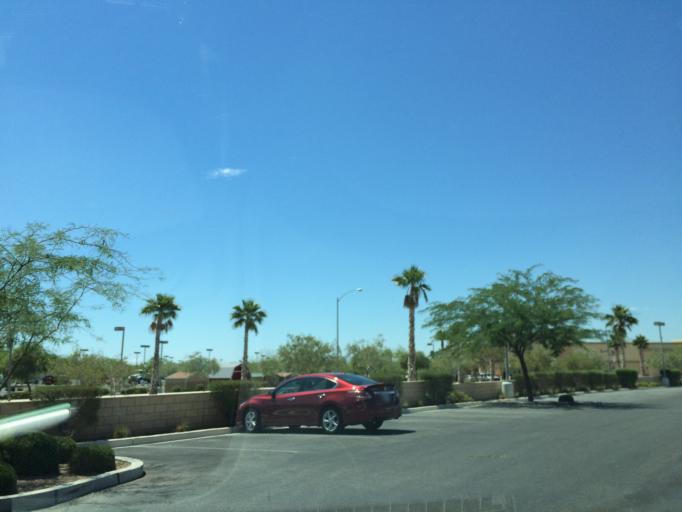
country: US
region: Nevada
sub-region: Clark County
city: Nellis Air Force Base
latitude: 36.2867
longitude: -115.1328
